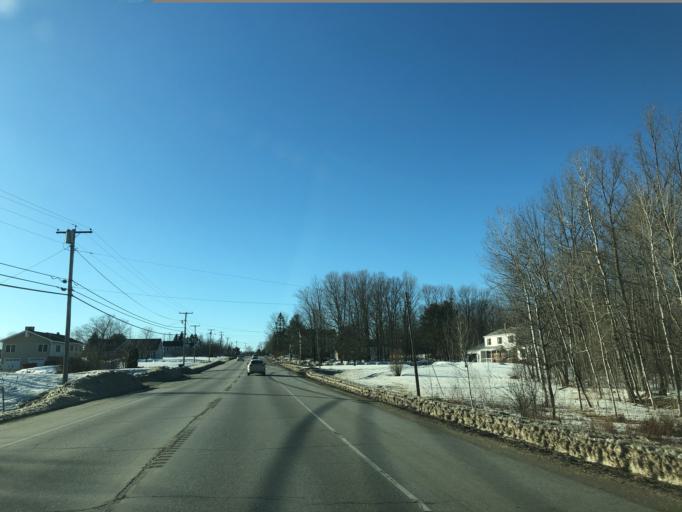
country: US
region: Maine
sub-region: Penobscot County
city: Kenduskeag
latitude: 44.9868
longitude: -69.0093
